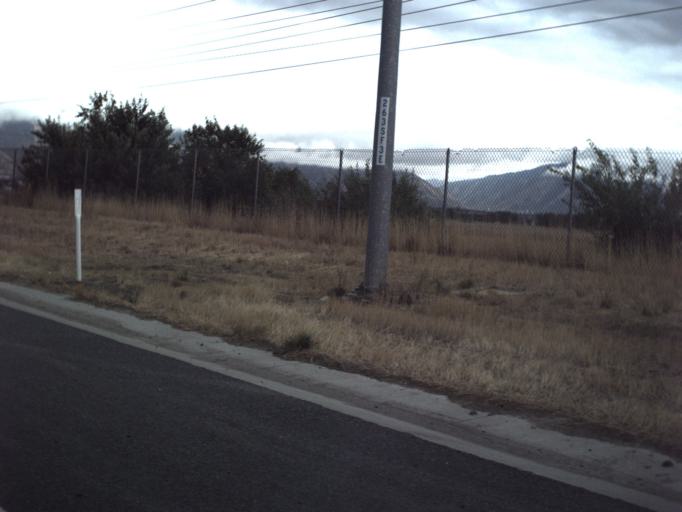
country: US
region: Utah
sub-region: Utah County
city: Provo
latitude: 40.2041
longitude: -111.6588
